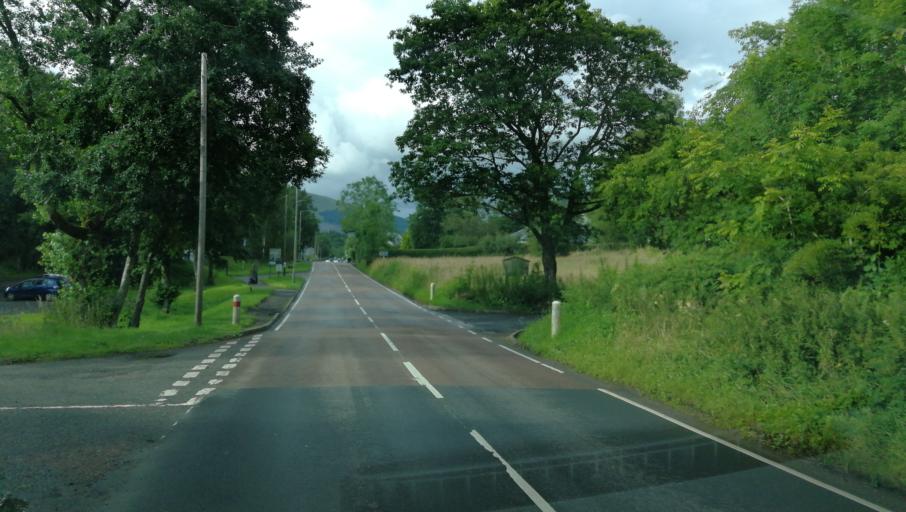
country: GB
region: Scotland
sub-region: Stirling
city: Callander
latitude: 56.3213
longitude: -4.3285
